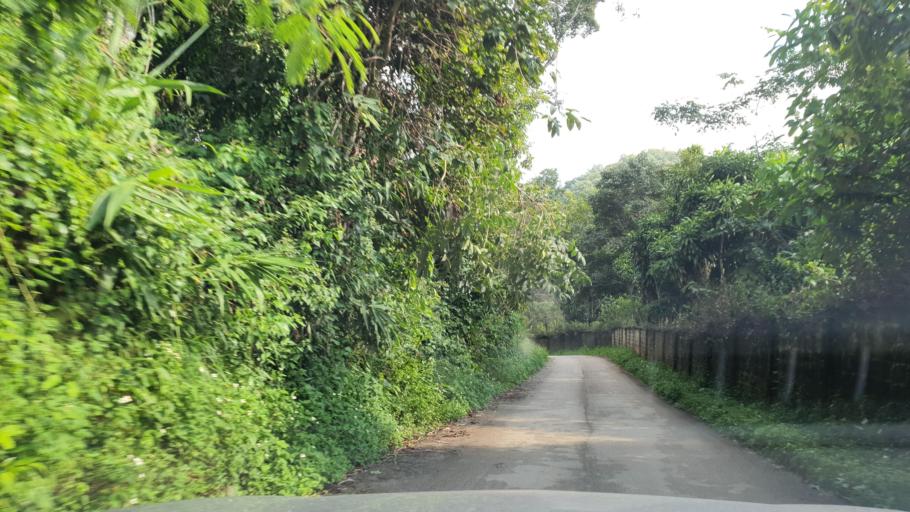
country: TH
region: Chiang Mai
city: Mae On
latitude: 18.9262
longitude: 99.3116
